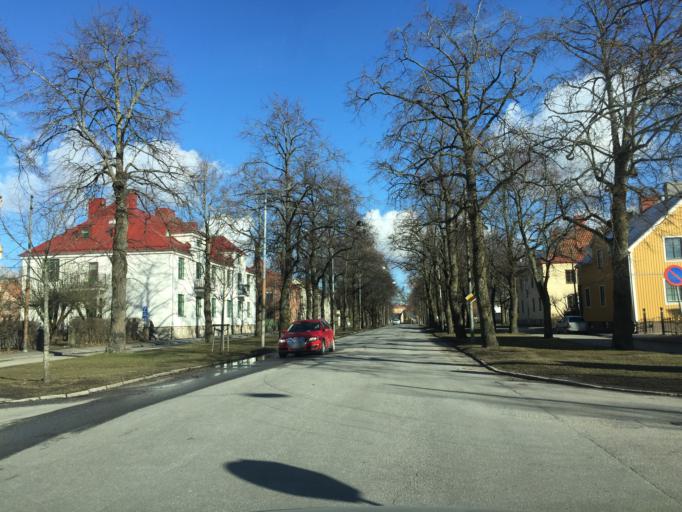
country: SE
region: OErebro
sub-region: Orebro Kommun
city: Orebro
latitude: 59.2686
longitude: 15.2353
